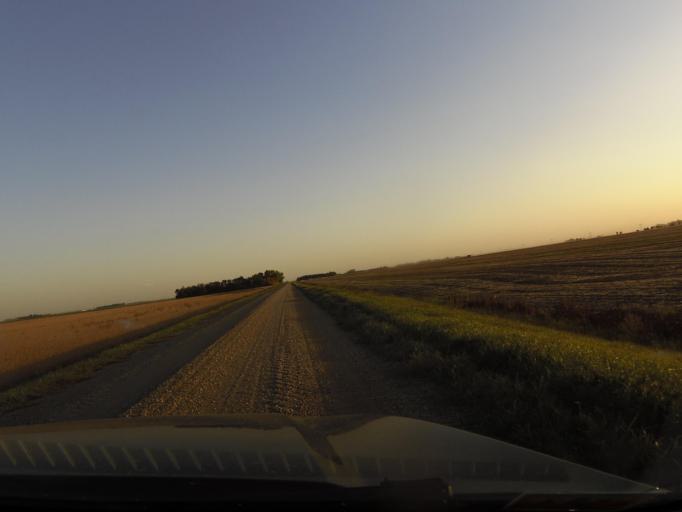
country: US
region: North Dakota
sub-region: Walsh County
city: Grafton
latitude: 48.3960
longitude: -97.2556
